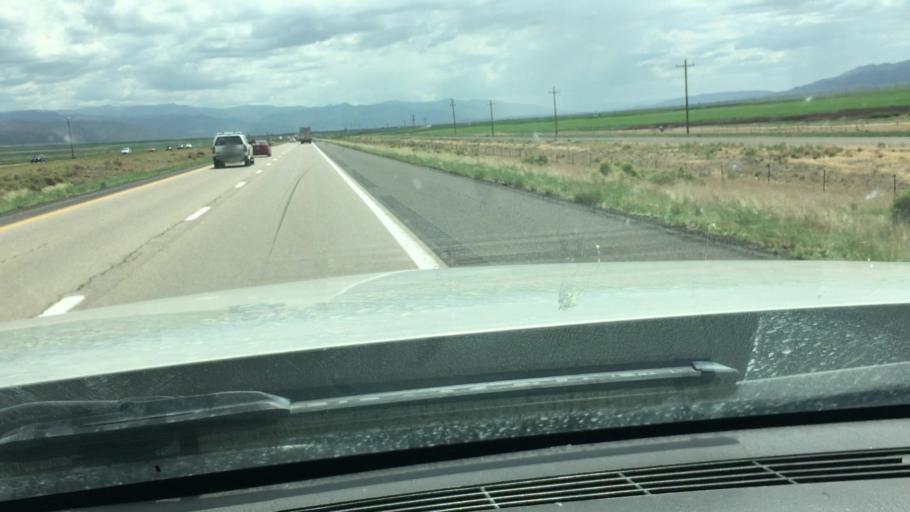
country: US
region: Utah
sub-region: Beaver County
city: Beaver
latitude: 38.0499
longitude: -112.7006
